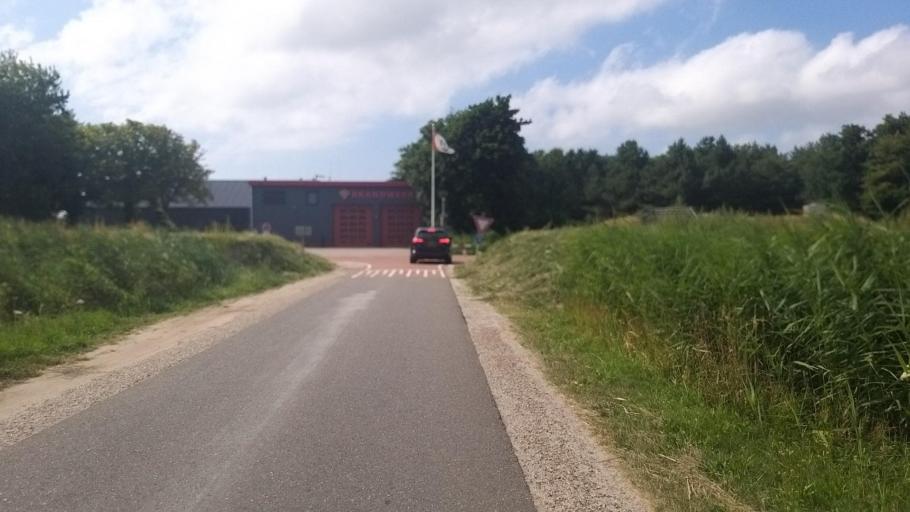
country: NL
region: North Holland
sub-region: Gemeente Texel
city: Den Burg
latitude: 53.1469
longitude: 4.8614
